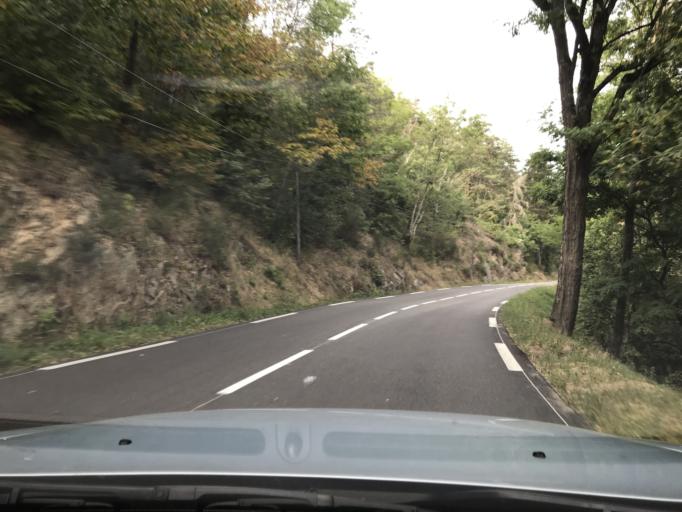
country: FR
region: Rhone-Alpes
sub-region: Departement de l'Ardeche
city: Lamastre
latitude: 44.9841
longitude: 4.6089
